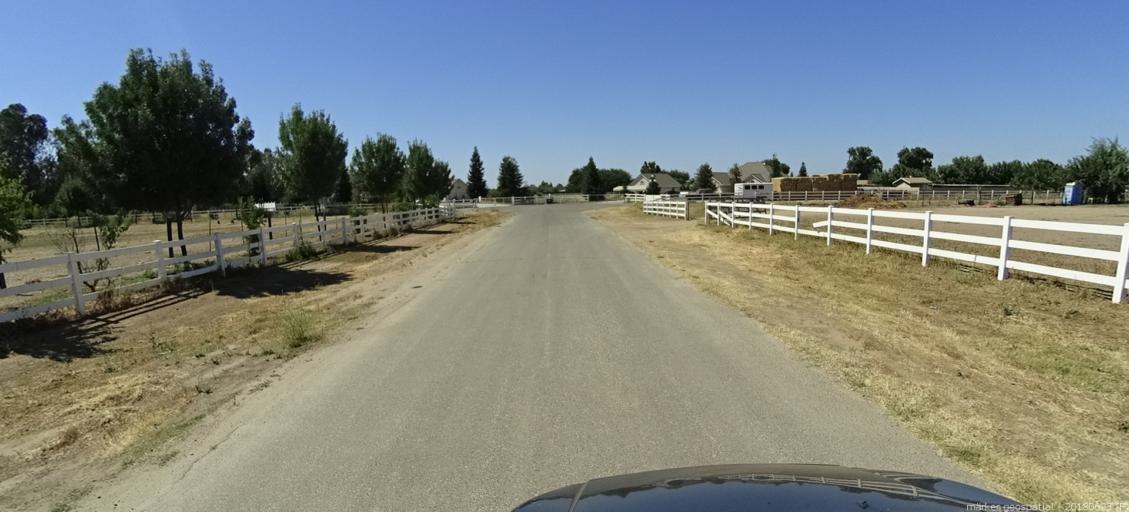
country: US
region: California
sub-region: Madera County
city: Parksdale
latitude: 36.9659
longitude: -120.0251
